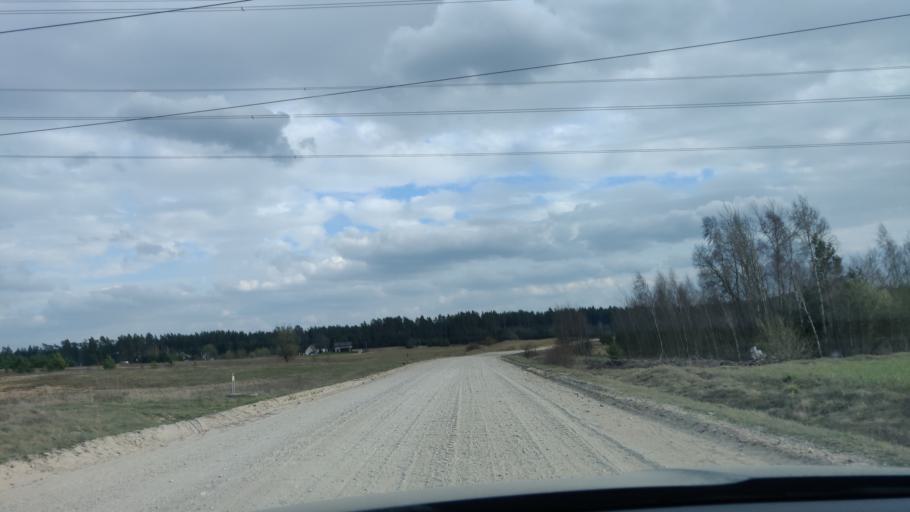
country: LT
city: Lentvaris
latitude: 54.6074
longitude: 25.0743
